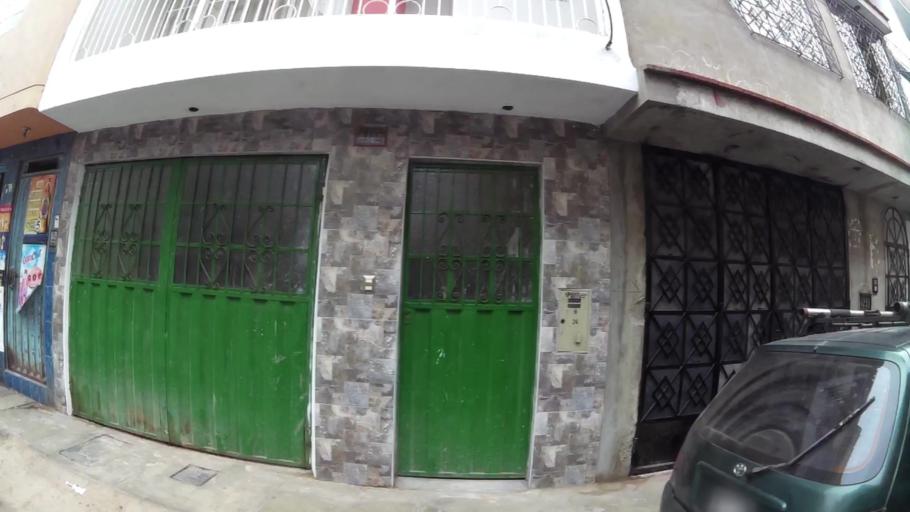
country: PE
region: Lima
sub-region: Lima
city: Surco
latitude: -12.1502
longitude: -77.0127
